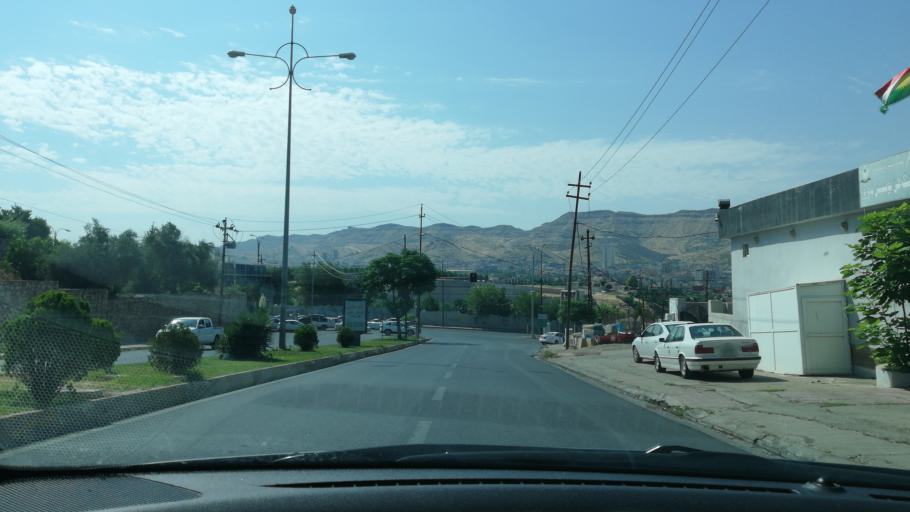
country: IQ
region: Dahuk
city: Dihok
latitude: 36.8614
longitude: 42.9843
